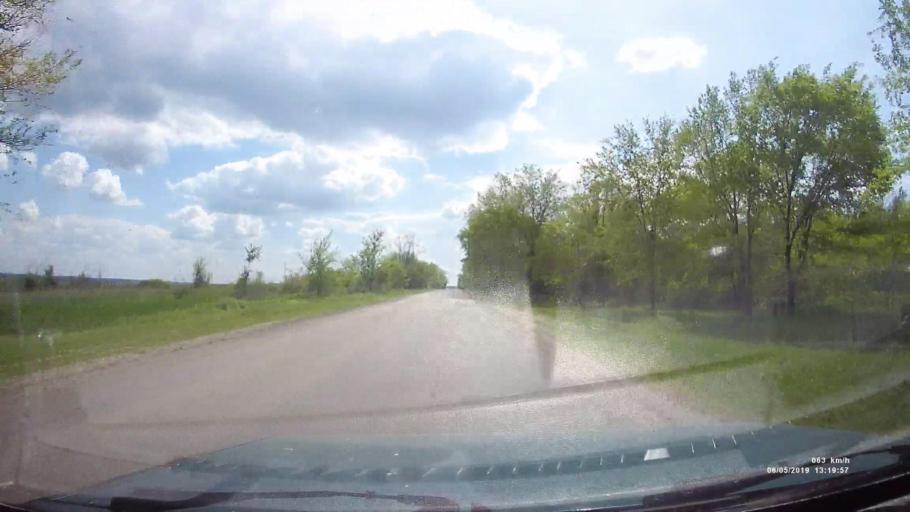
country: RU
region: Rostov
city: Ust'-Donetskiy
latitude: 47.7208
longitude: 40.9122
